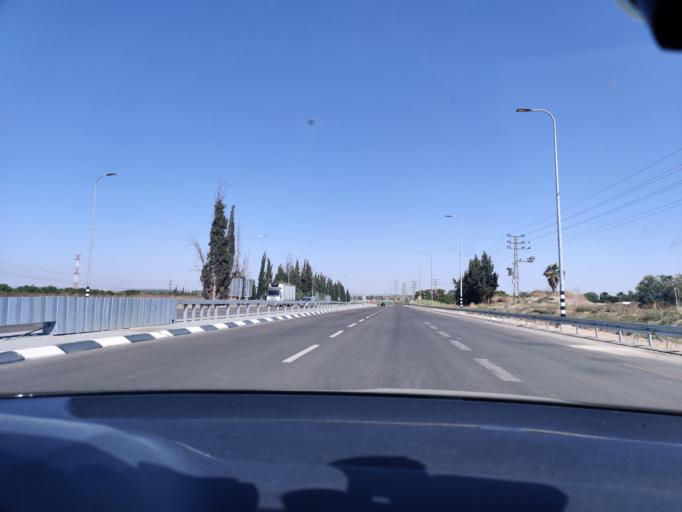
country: IL
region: Southern District
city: Qiryat Gat
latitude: 31.6078
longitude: 34.7877
